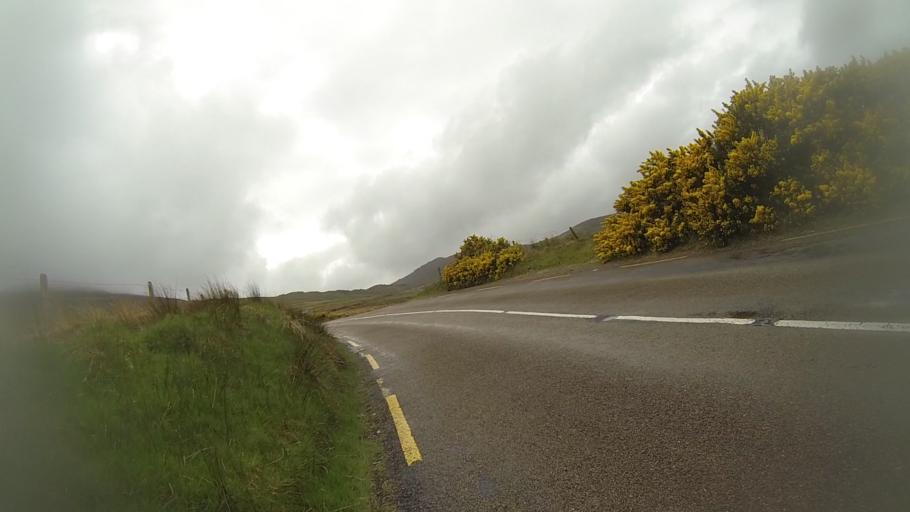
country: IE
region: Munster
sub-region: Ciarrai
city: Kenmare
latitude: 51.8804
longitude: -9.7969
